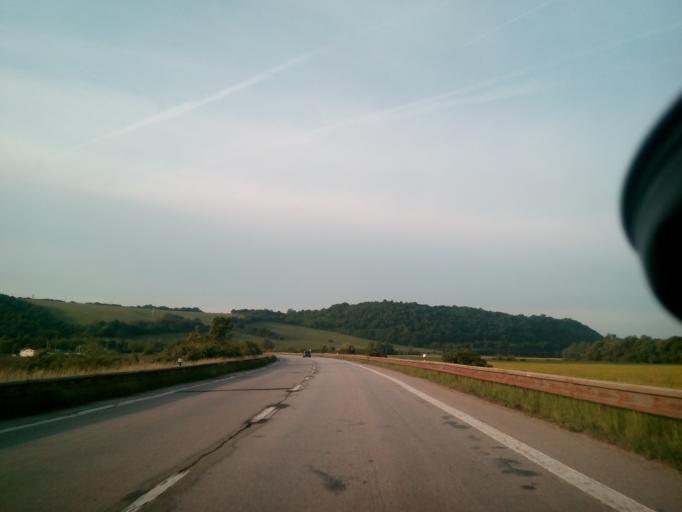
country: SK
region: Kosicky
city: Roznava
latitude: 48.5390
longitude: 20.3954
